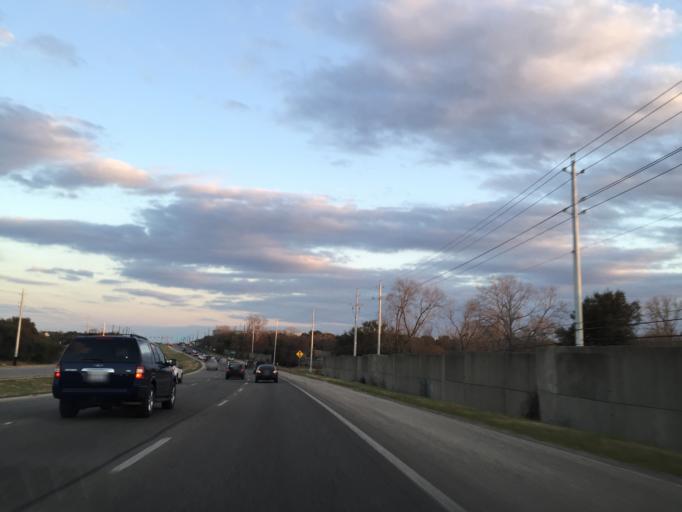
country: US
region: Texas
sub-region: Williamson County
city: Jollyville
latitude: 30.4408
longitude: -97.7405
